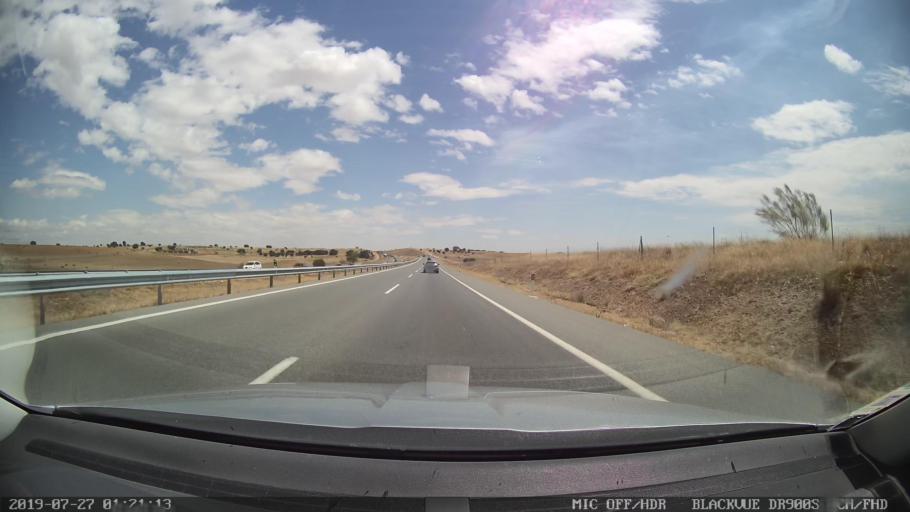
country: ES
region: Castille-La Mancha
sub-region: Province of Toledo
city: Quismondo
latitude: 40.1188
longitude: -4.2841
